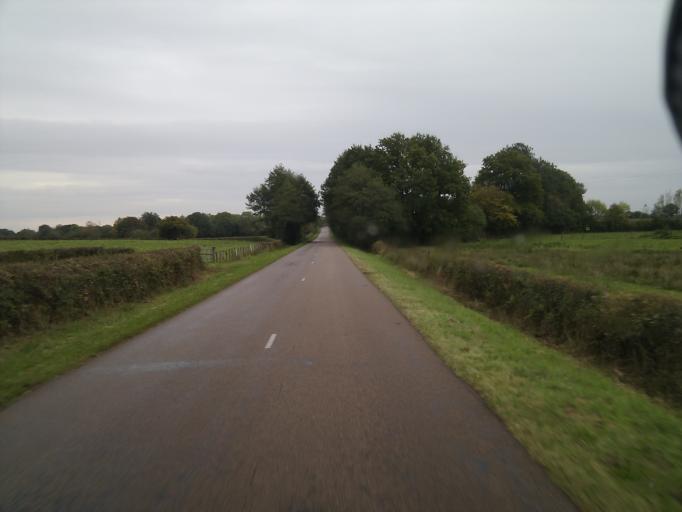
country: FR
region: Bourgogne
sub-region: Departement de la Cote-d'Or
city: Saulieu
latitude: 47.2782
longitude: 4.1950
